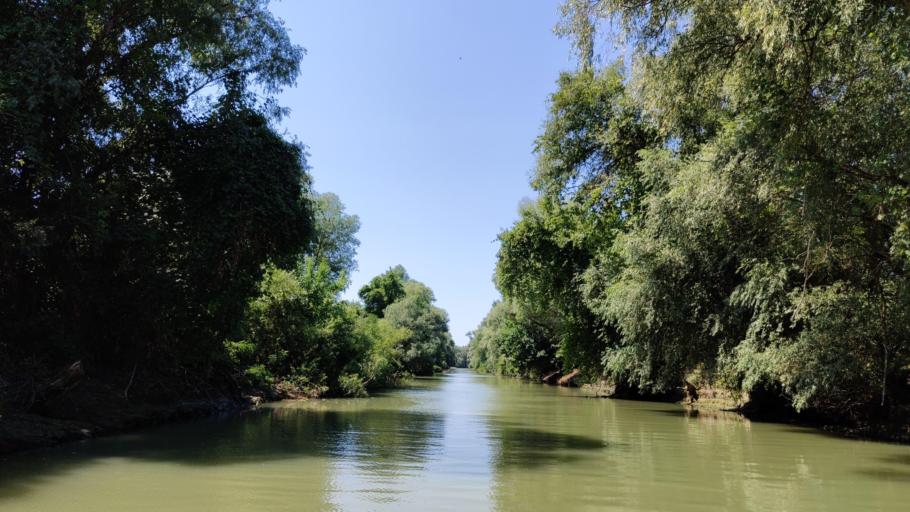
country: RO
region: Tulcea
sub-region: Comuna Pardina
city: Pardina
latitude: 45.2542
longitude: 28.9340
